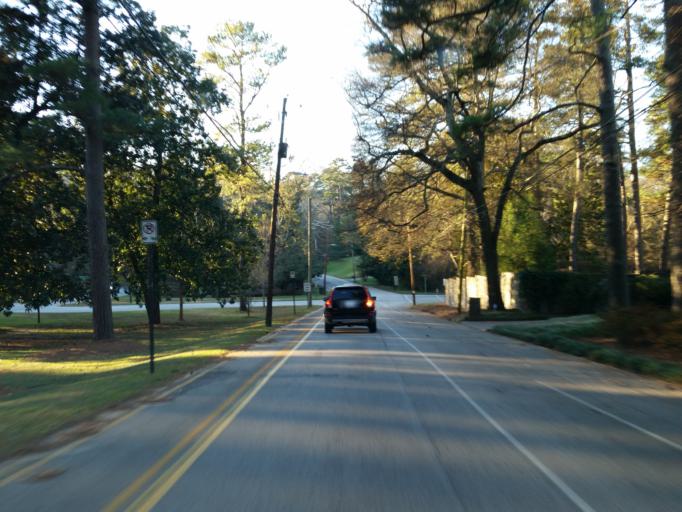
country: US
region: Georgia
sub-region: DeKalb County
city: Druid Hills
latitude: 33.8208
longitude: -84.3909
